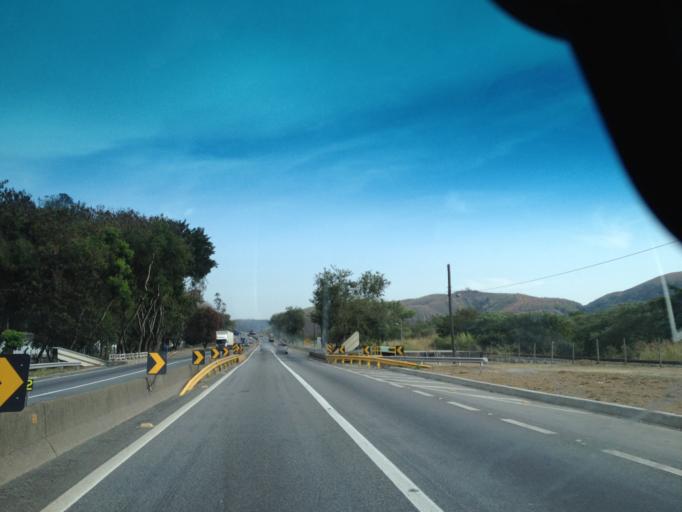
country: BR
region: Rio de Janeiro
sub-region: Barra Mansa
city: Barra Mansa
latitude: -22.5031
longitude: -44.2271
